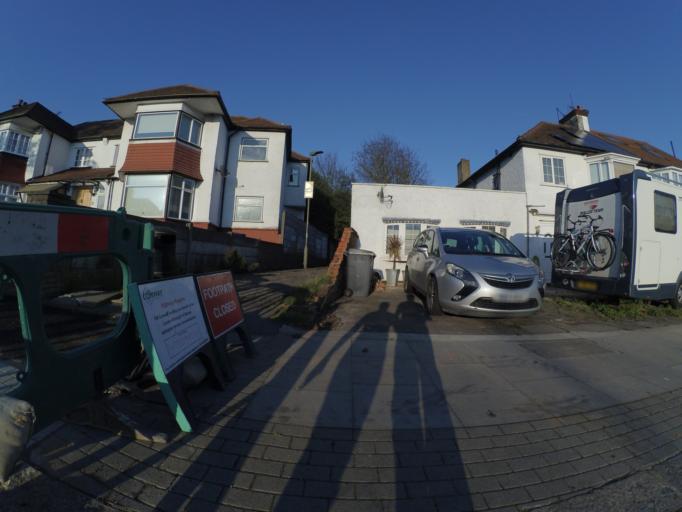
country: GB
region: England
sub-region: Greater London
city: Hendon
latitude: 51.5793
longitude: -0.2210
